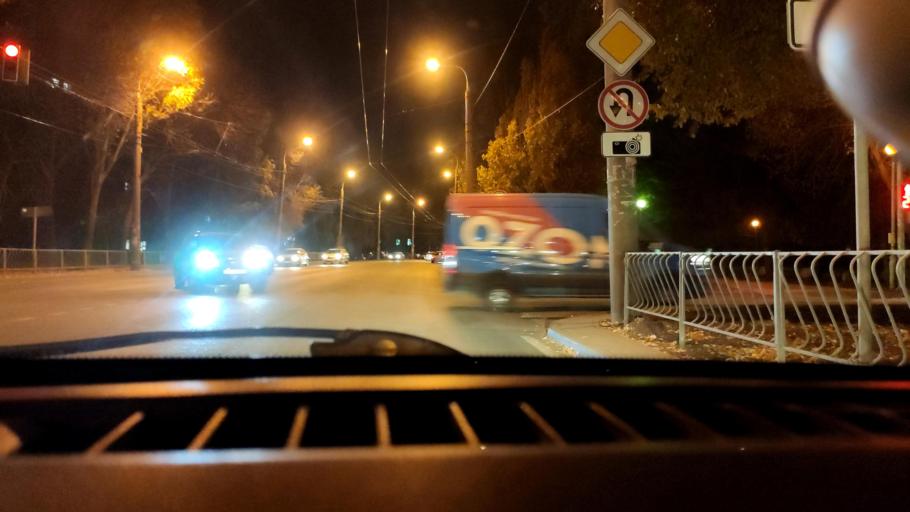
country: RU
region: Samara
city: Samara
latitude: 53.2383
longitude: 50.2269
